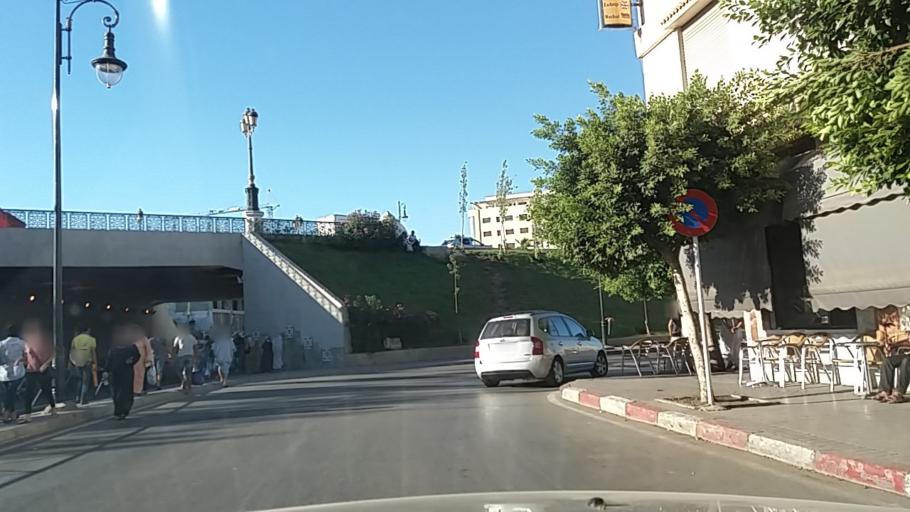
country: MA
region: Tanger-Tetouan
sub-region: Tanger-Assilah
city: Tangier
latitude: 35.7590
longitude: -5.8218
